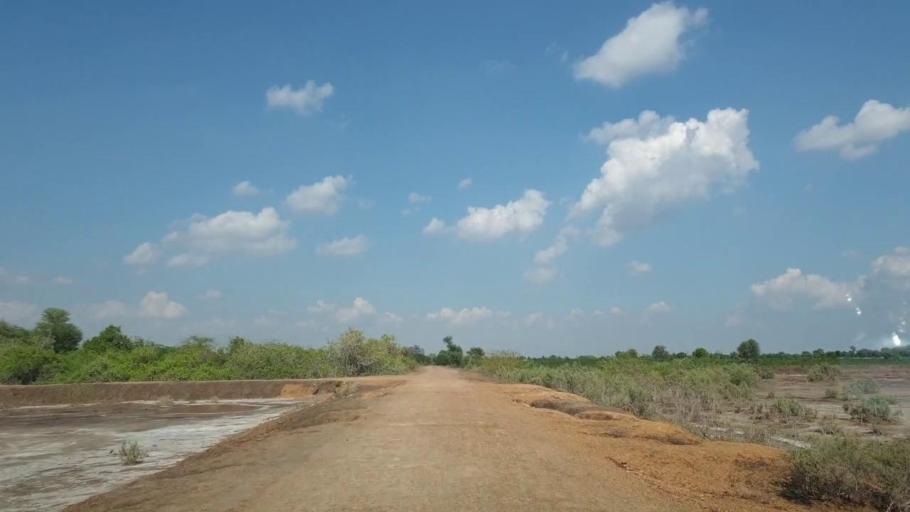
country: PK
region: Sindh
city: Pithoro
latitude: 25.6026
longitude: 69.3822
